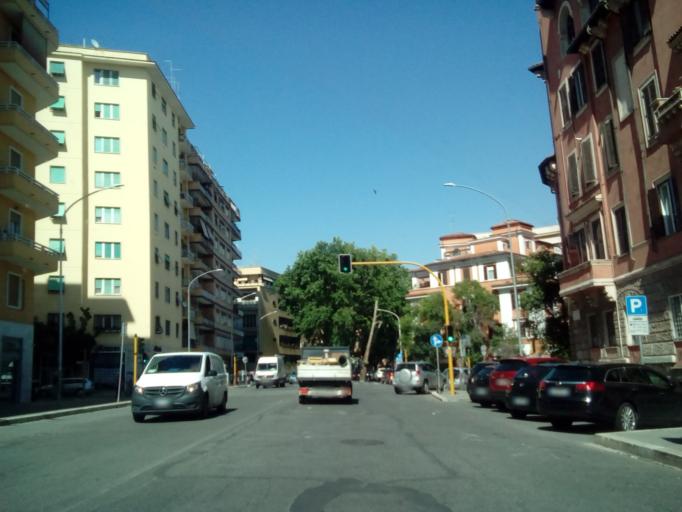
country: IT
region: Latium
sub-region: Citta metropolitana di Roma Capitale
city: Rome
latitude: 41.8808
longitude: 12.5090
